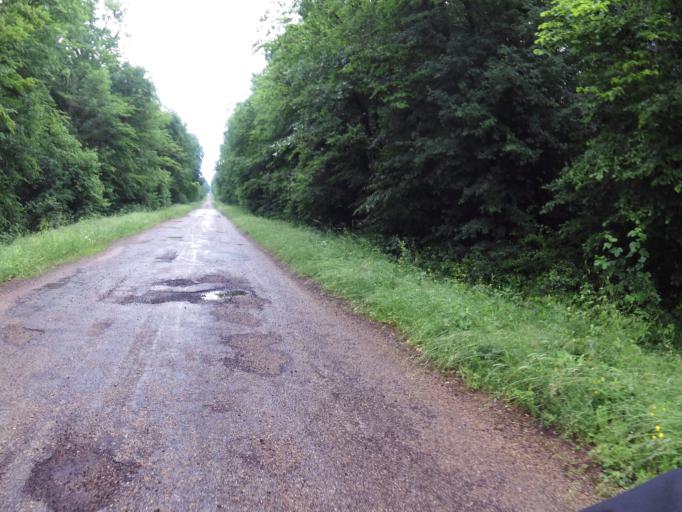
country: FR
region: Champagne-Ardenne
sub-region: Departement de la Marne
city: Sermaize-les-Bains
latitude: 48.7586
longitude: 4.9520
